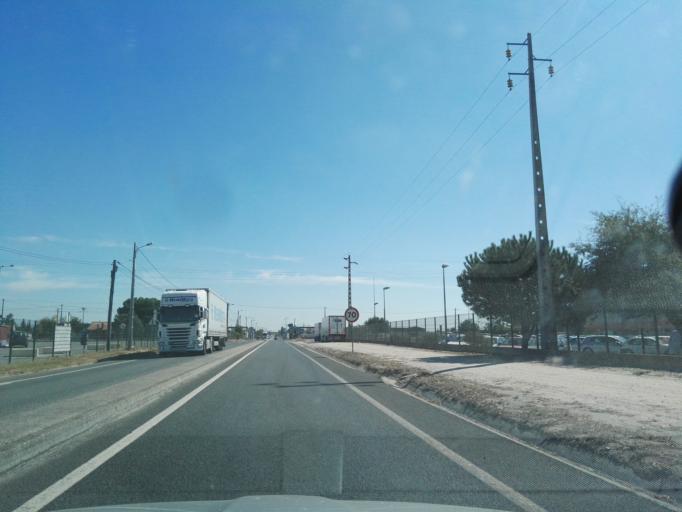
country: PT
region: Santarem
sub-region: Benavente
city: Samora Correia
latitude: 38.9187
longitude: -8.8729
